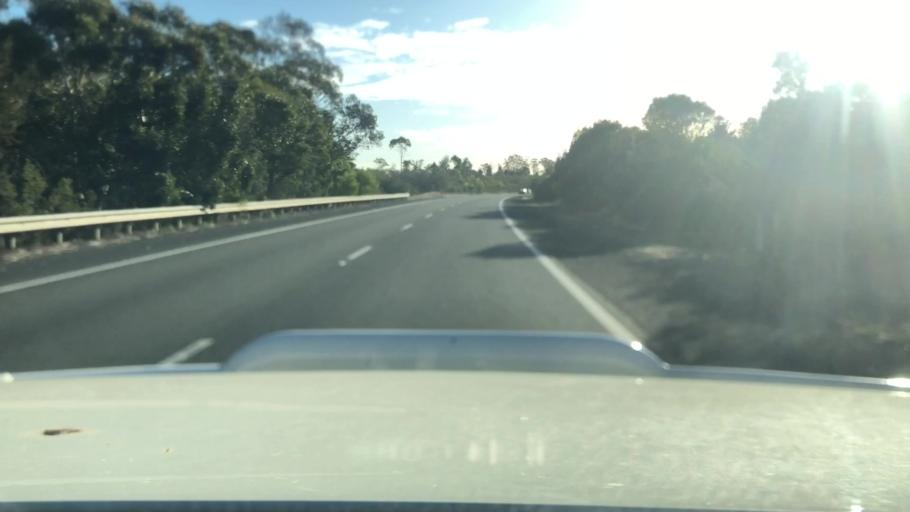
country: AU
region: New South Wales
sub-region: Wingecarribee
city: Colo Vale
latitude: -34.3530
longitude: 150.5441
